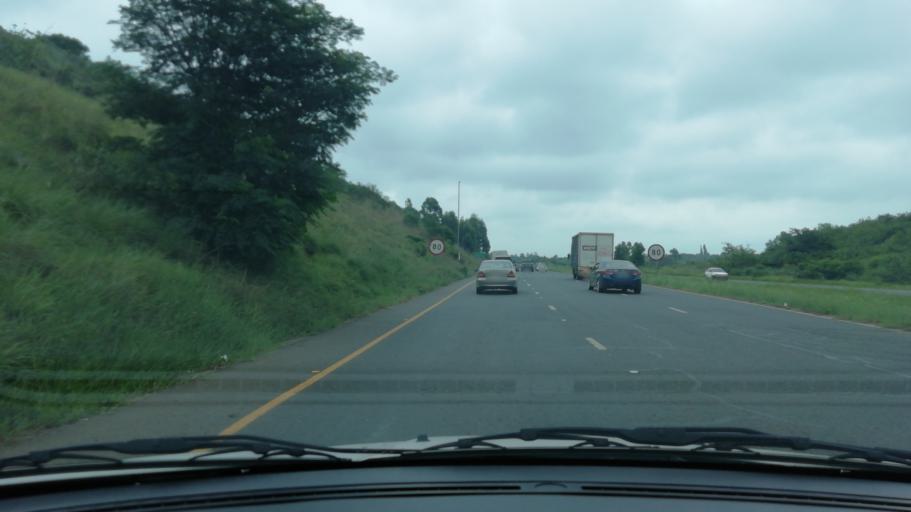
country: ZA
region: KwaZulu-Natal
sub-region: uThungulu District Municipality
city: Empangeni
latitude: -28.7685
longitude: 31.9287
